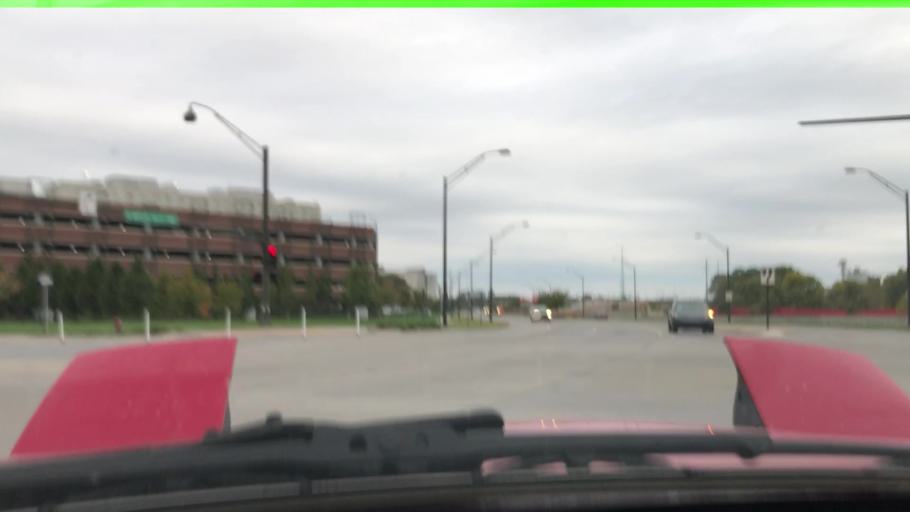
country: US
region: Nebraska
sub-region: Lancaster County
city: Lincoln
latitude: 40.8209
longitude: -96.6927
